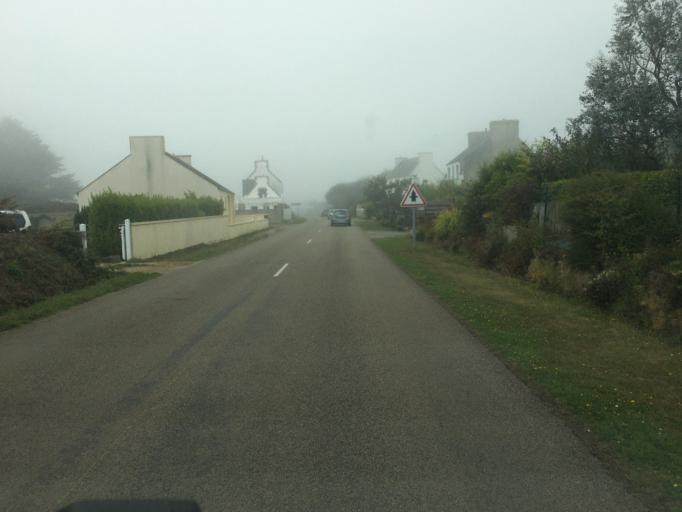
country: FR
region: Brittany
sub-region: Departement du Finistere
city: Plogoff
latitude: 48.0565
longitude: -4.6874
